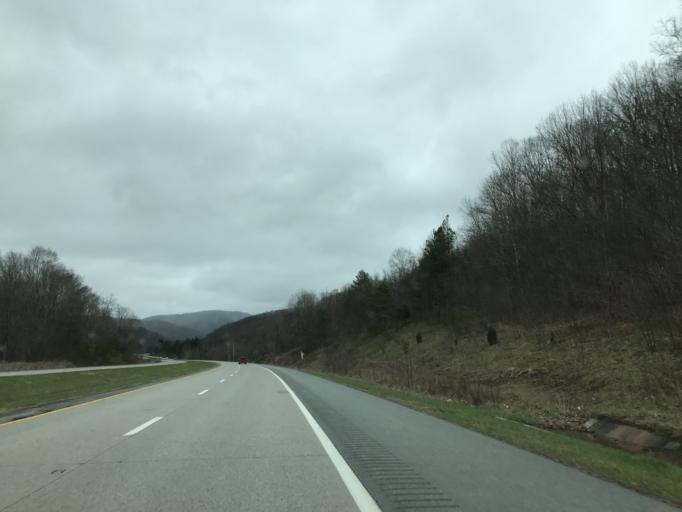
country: US
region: West Virginia
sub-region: Summers County
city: Hinton
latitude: 37.7955
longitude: -80.8502
